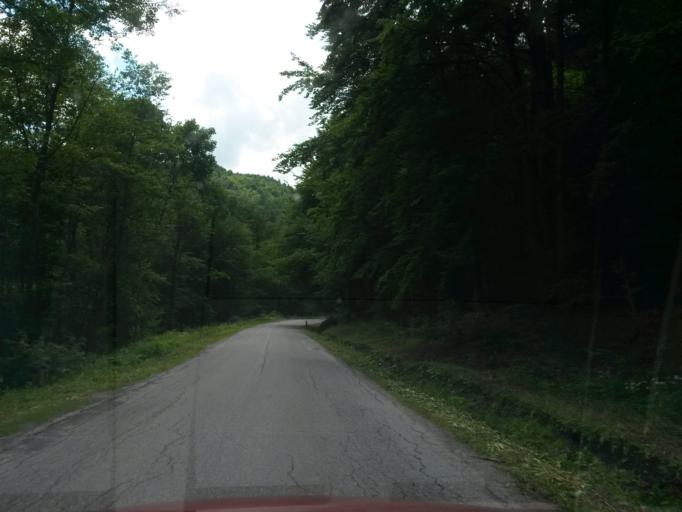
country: SK
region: Kosicky
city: Gelnica
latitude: 48.9223
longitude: 21.0396
